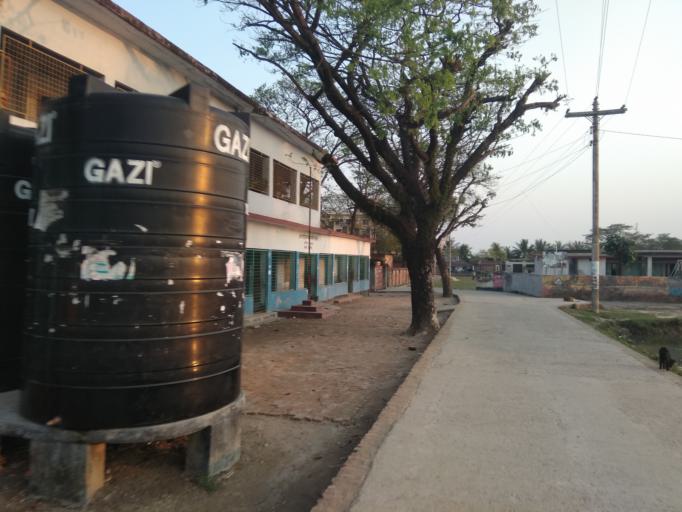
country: BD
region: Khulna
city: Satkhira
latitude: 22.5475
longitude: 89.1774
